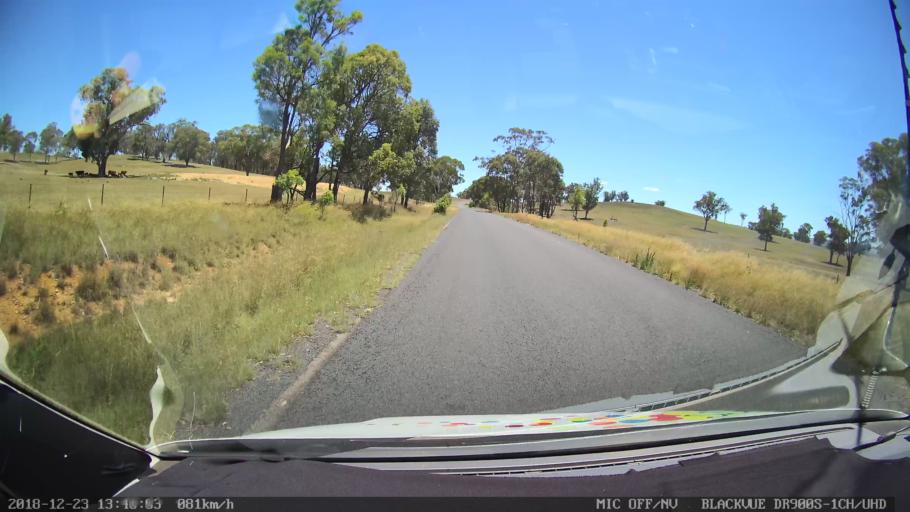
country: AU
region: New South Wales
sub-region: Armidale Dumaresq
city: Armidale
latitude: -30.4635
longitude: 151.1951
